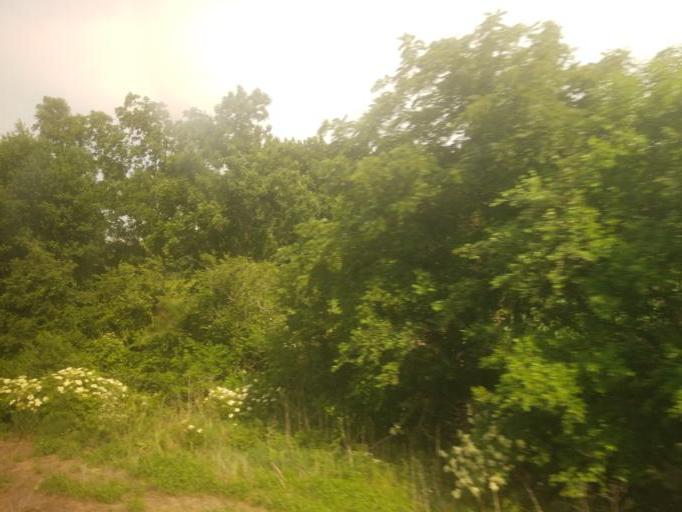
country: US
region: Illinois
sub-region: Knox County
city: Galesburg
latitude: 40.9046
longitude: -90.4372
